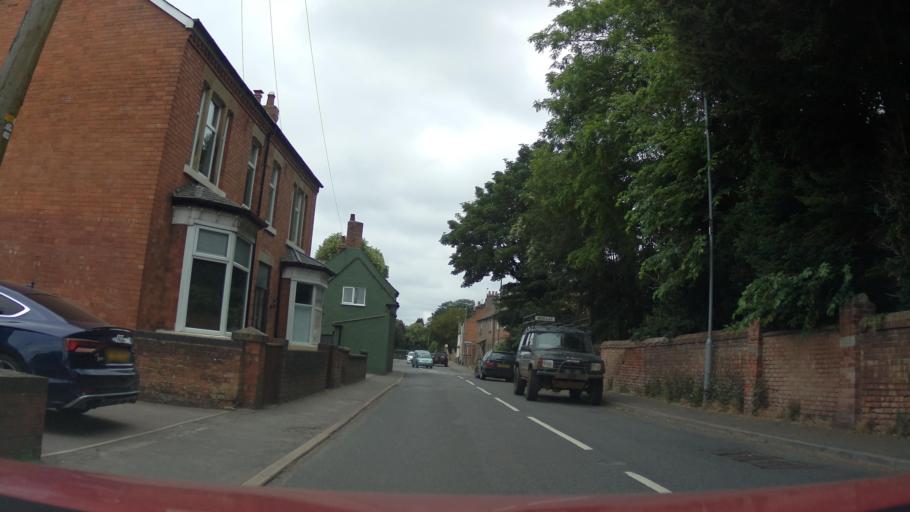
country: GB
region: England
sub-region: Leicestershire
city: Asfordby
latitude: 52.7640
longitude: -0.9534
